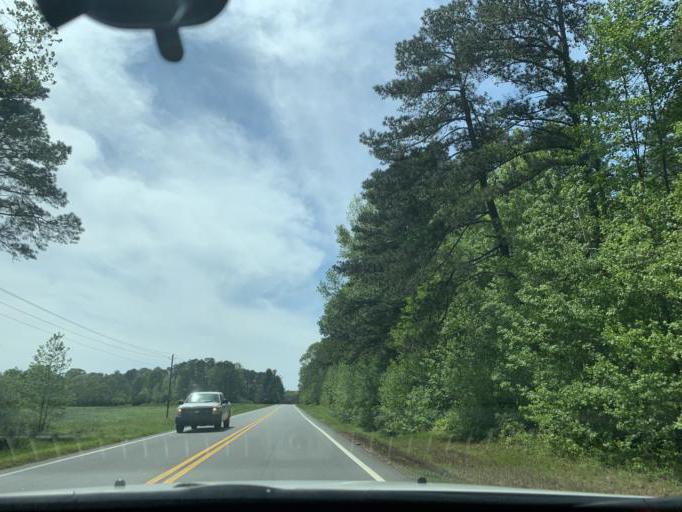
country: US
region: Georgia
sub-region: Forsyth County
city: Cumming
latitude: 34.2503
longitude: -84.1054
